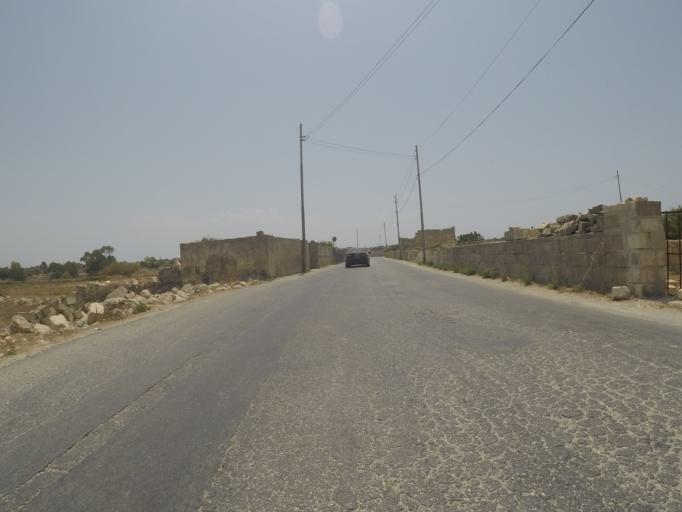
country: MT
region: Is-Siggiewi
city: Siggiewi
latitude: 35.8486
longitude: 14.4338
